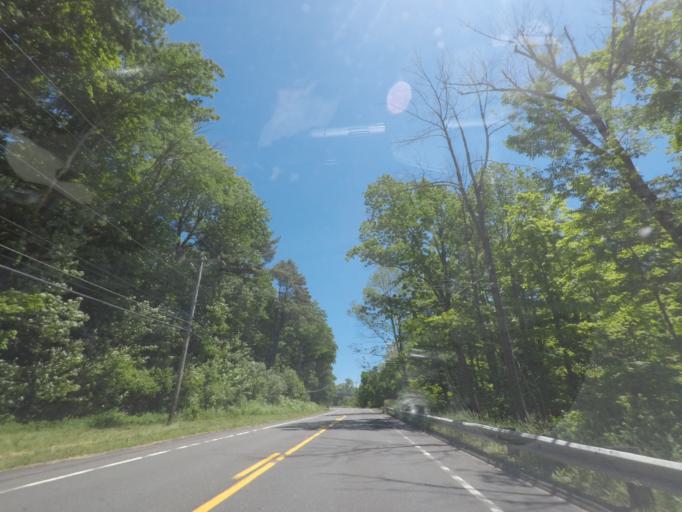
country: US
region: Massachusetts
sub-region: Berkshire County
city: Otis
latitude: 42.2595
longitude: -73.0904
